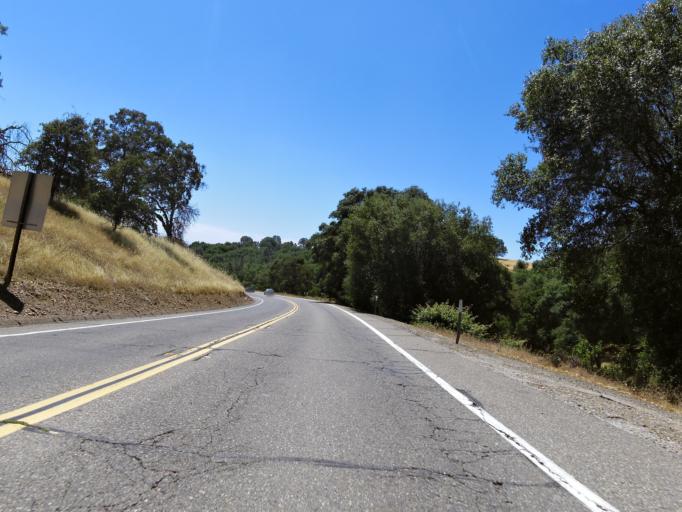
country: US
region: California
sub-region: Mariposa County
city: Mariposa
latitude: 37.4731
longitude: -119.9712
